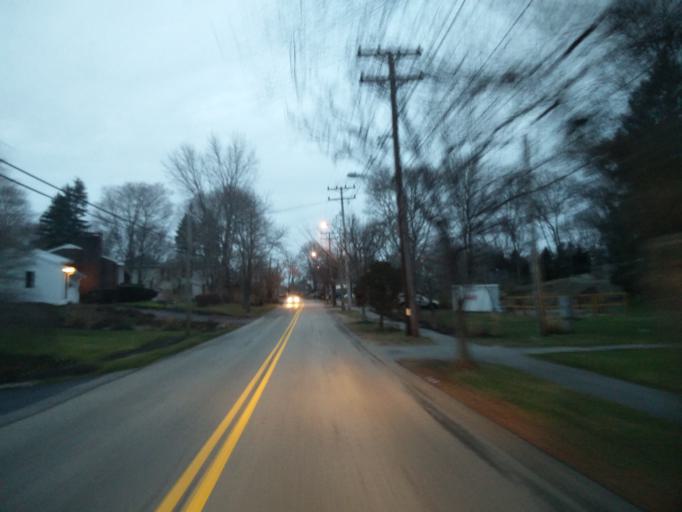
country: US
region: Massachusetts
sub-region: Plymouth County
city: Hingham
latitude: 42.2485
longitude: -70.8625
